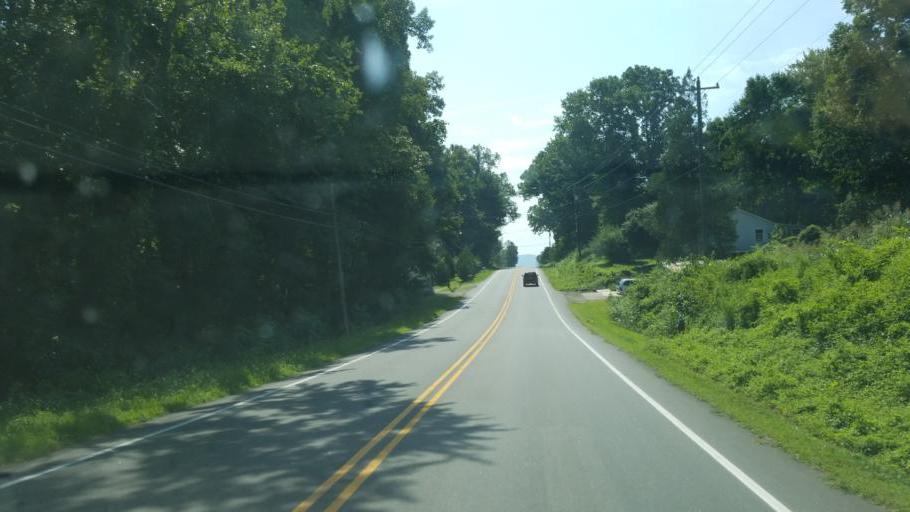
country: US
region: North Carolina
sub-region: Burke County
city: Morganton
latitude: 35.7593
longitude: -81.7317
